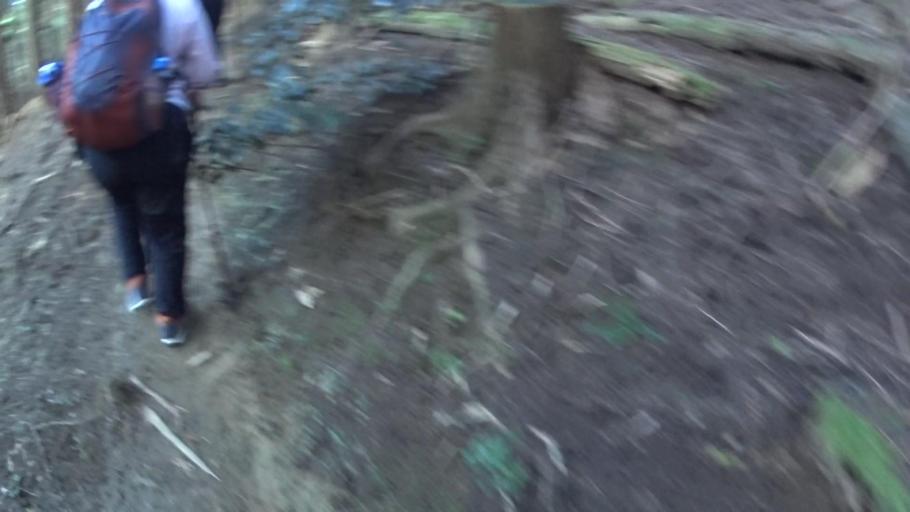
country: JP
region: Shiga Prefecture
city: Kitahama
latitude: 35.1030
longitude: 135.8434
